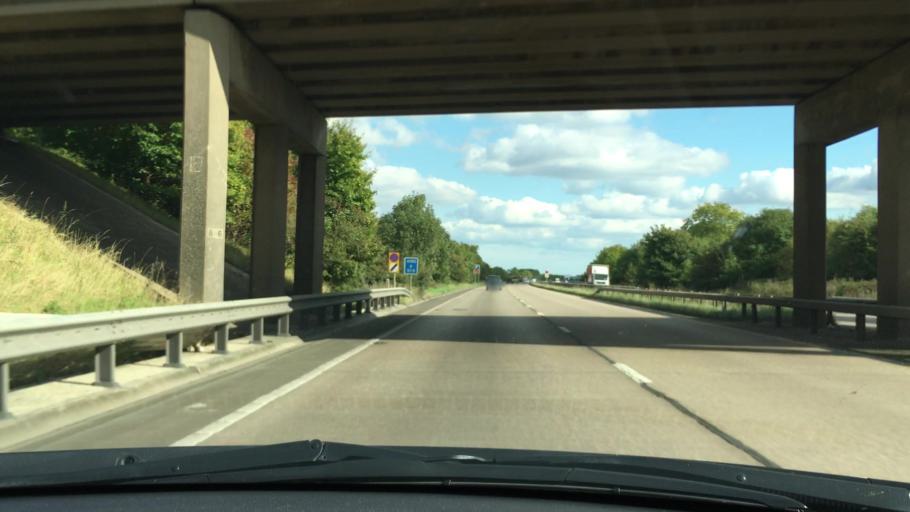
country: GB
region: England
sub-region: North East Lincolnshire
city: Healing
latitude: 53.5942
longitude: -0.1739
